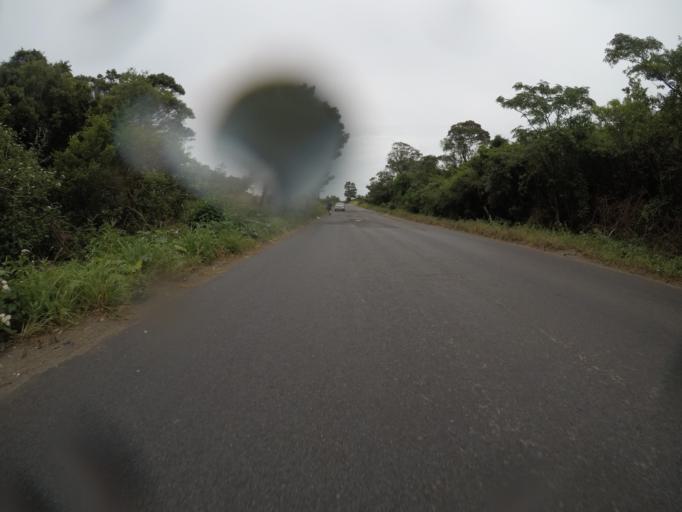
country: ZA
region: Eastern Cape
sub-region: Buffalo City Metropolitan Municipality
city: East London
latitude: -32.9792
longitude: 27.8268
